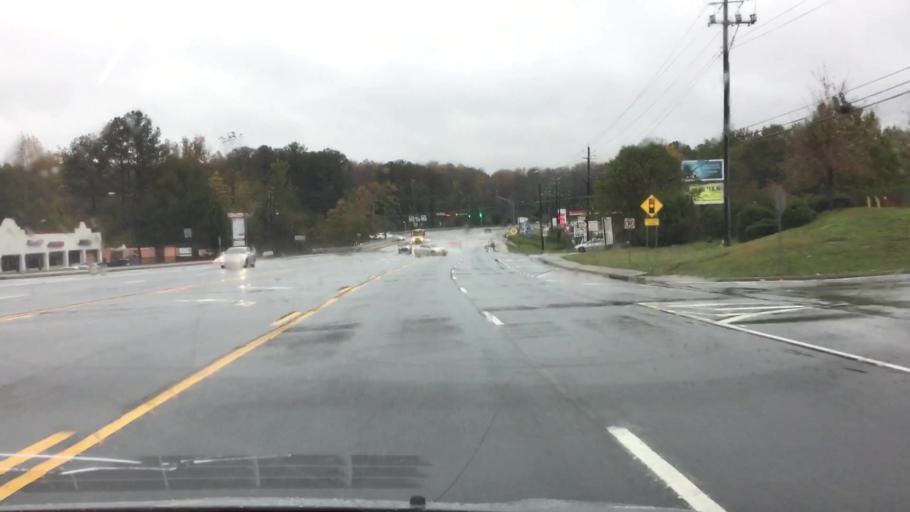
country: US
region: Georgia
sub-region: DeKalb County
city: Panthersville
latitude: 33.6850
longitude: -84.2002
